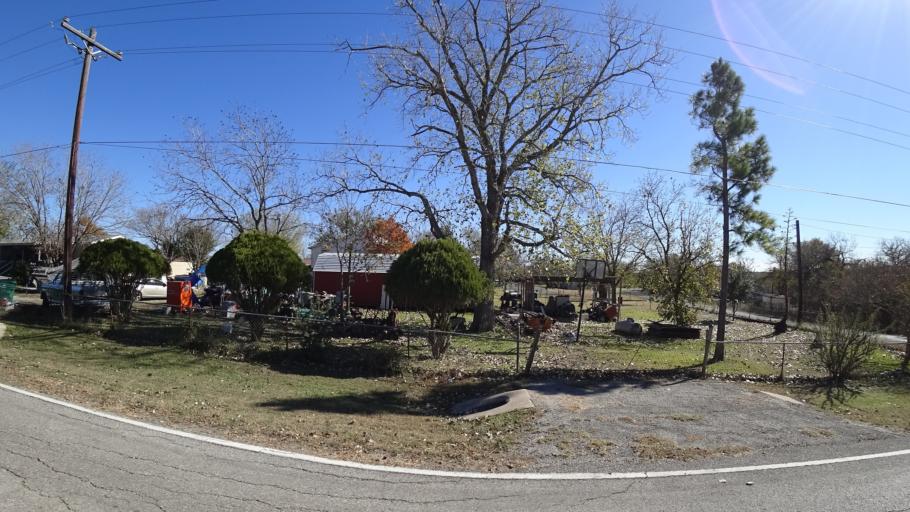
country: US
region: Texas
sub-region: Travis County
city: Garfield
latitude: 30.1291
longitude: -97.6161
